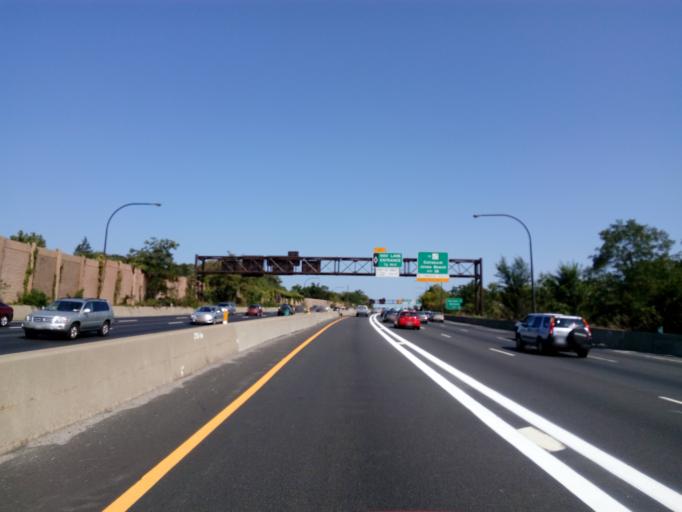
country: US
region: New York
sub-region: Nassau County
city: Roslyn Heights
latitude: 40.7849
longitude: -73.6413
